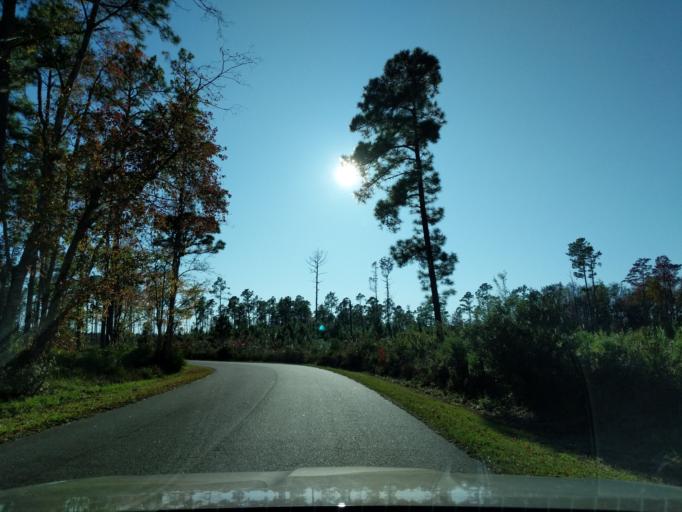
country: US
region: Georgia
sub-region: Charlton County
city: Folkston
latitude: 30.7197
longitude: -82.1401
